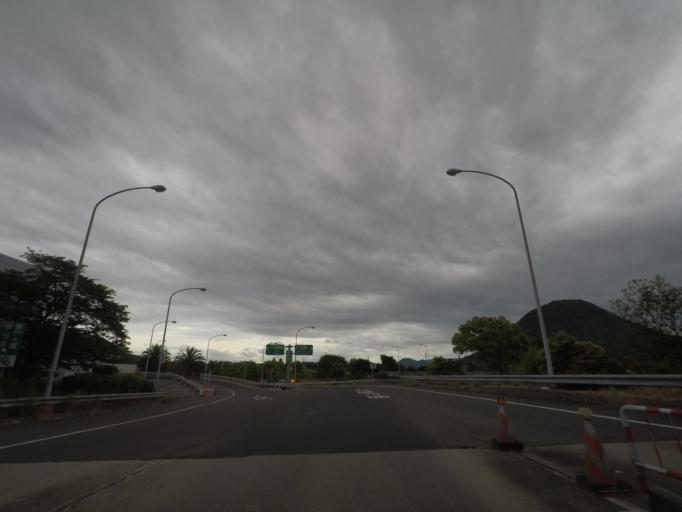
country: JP
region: Kagawa
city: Sakaidecho
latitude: 34.2966
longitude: 133.8428
